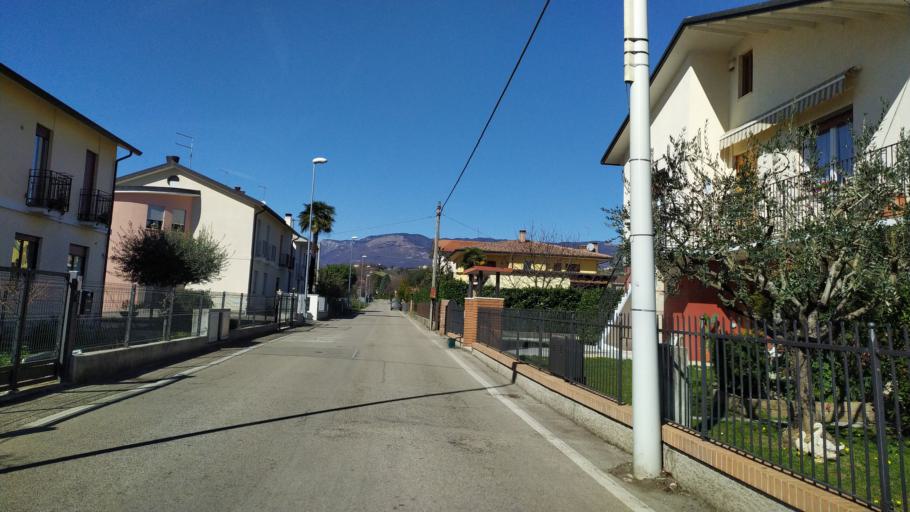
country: IT
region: Veneto
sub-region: Provincia di Vicenza
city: Breganze
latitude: 45.7028
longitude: 11.5731
